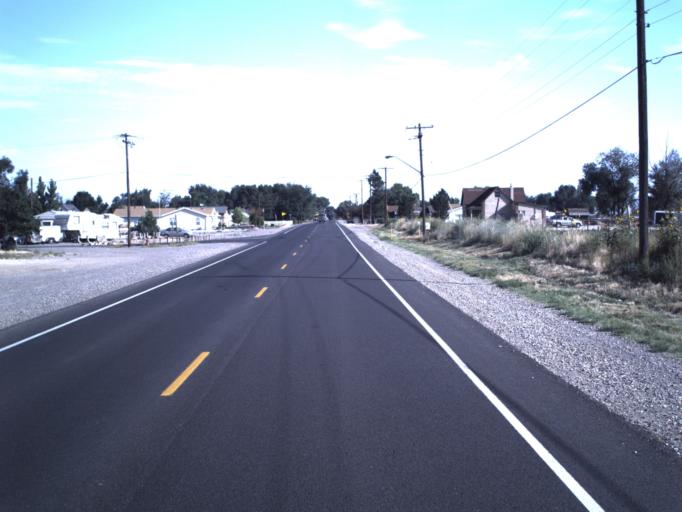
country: US
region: Utah
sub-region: Sevier County
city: Salina
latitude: 39.0013
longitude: -111.8615
